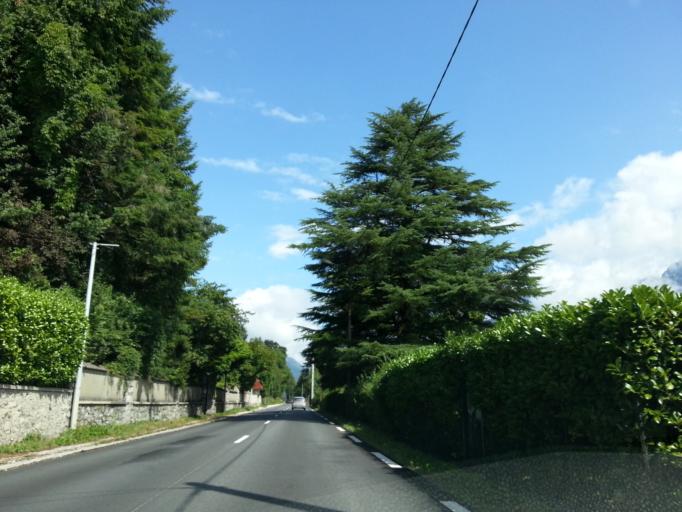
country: FR
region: Rhone-Alpes
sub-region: Departement de la Haute-Savoie
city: Doussard
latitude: 45.8002
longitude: 6.2126
